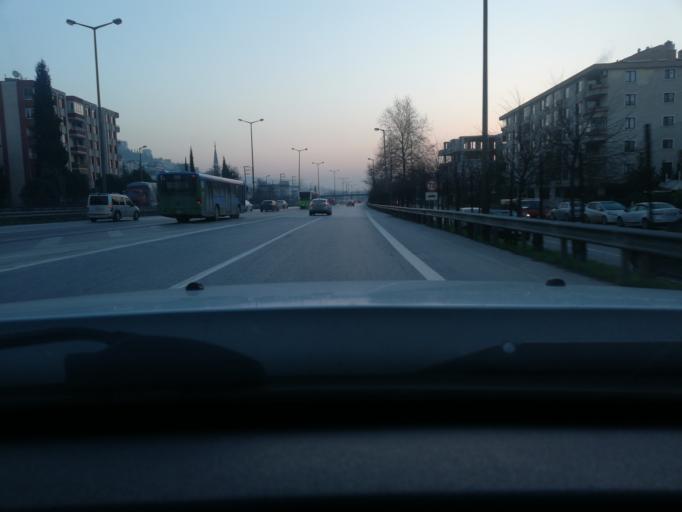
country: TR
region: Kocaeli
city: Izmit
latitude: 40.7628
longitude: 29.8802
